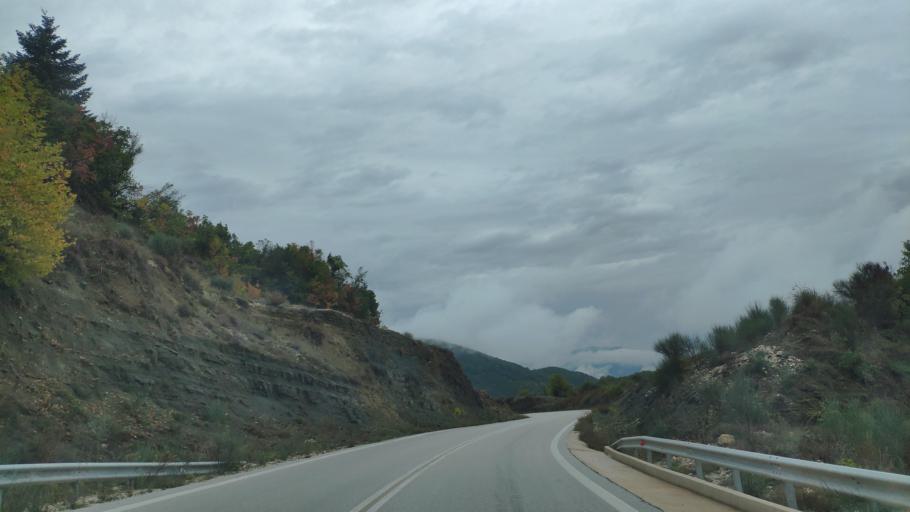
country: GR
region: Epirus
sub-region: Nomos Thesprotias
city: Paramythia
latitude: 39.4823
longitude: 20.6734
